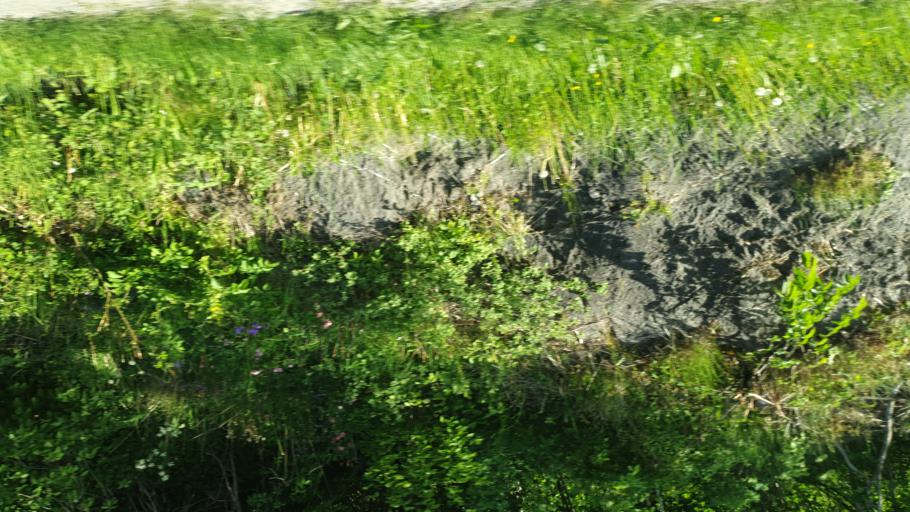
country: NO
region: Sor-Trondelag
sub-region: Rissa
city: Rissa
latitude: 63.4967
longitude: 10.0994
